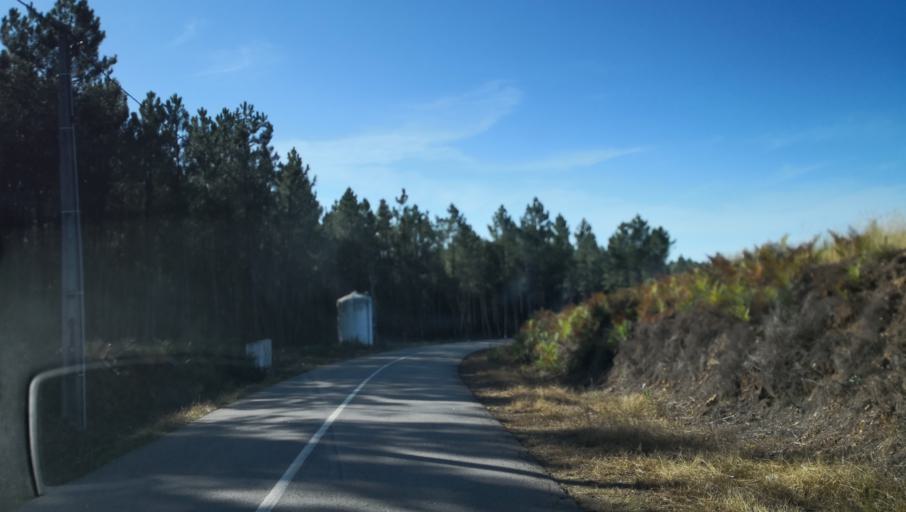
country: PT
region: Vila Real
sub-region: Sabrosa
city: Vilela
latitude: 41.2559
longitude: -7.6230
